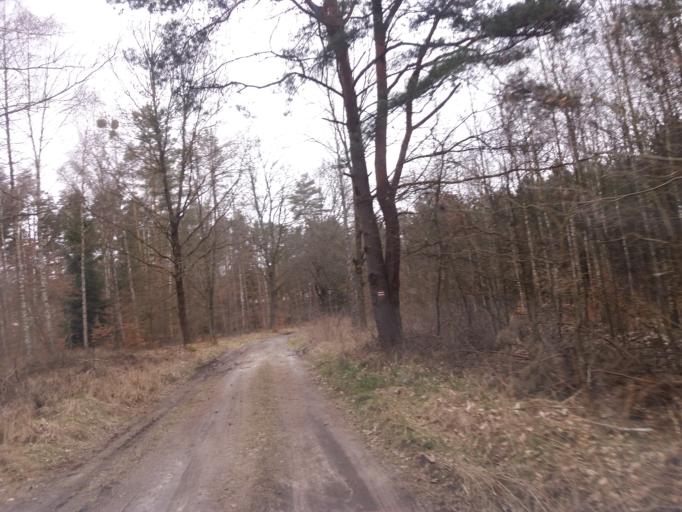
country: PL
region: West Pomeranian Voivodeship
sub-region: Powiat choszczenski
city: Drawno
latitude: 53.1799
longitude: 15.7821
